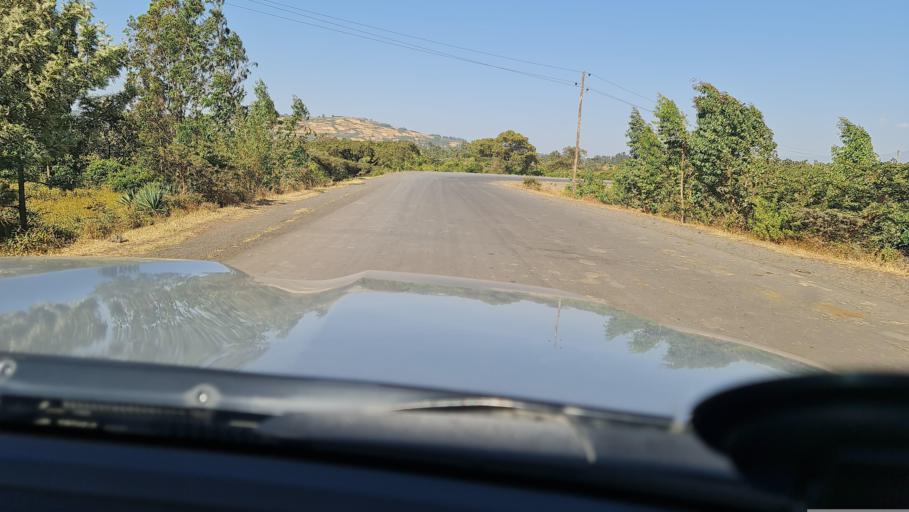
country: ET
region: Oromiya
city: Waliso
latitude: 8.5648
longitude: 37.9459
